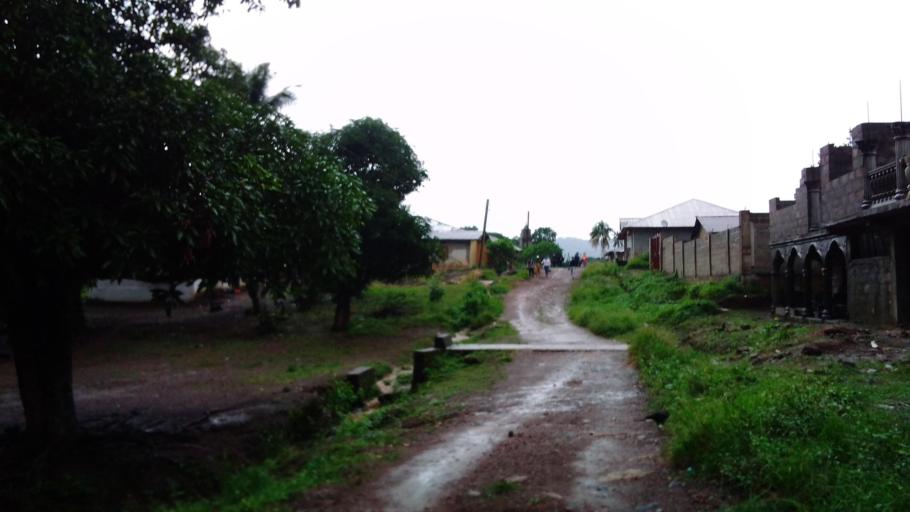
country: SL
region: Eastern Province
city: Kenema
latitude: 7.8805
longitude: -11.1800
